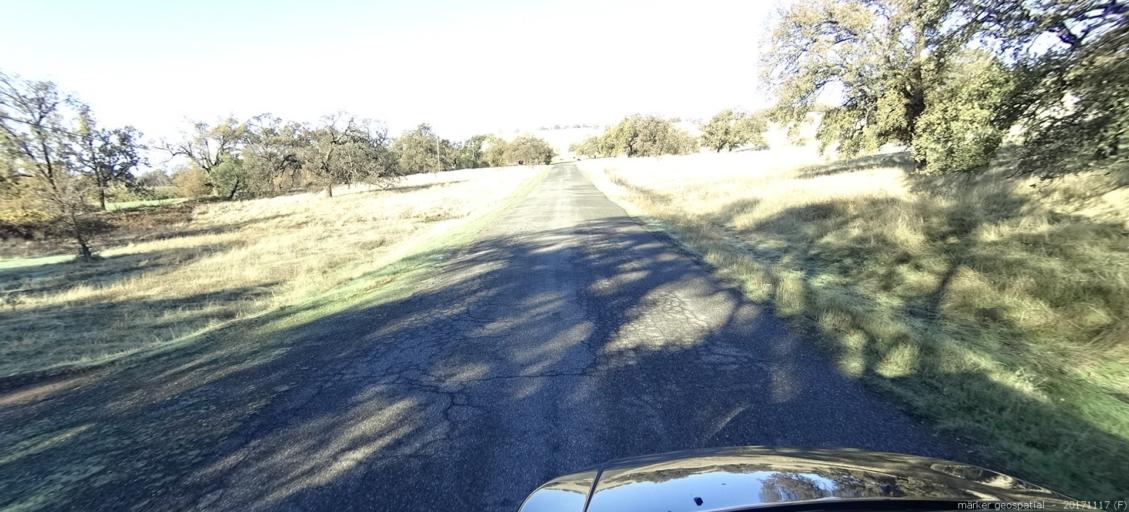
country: US
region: California
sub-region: Shasta County
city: Cottonwood
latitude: 40.3985
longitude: -122.1701
